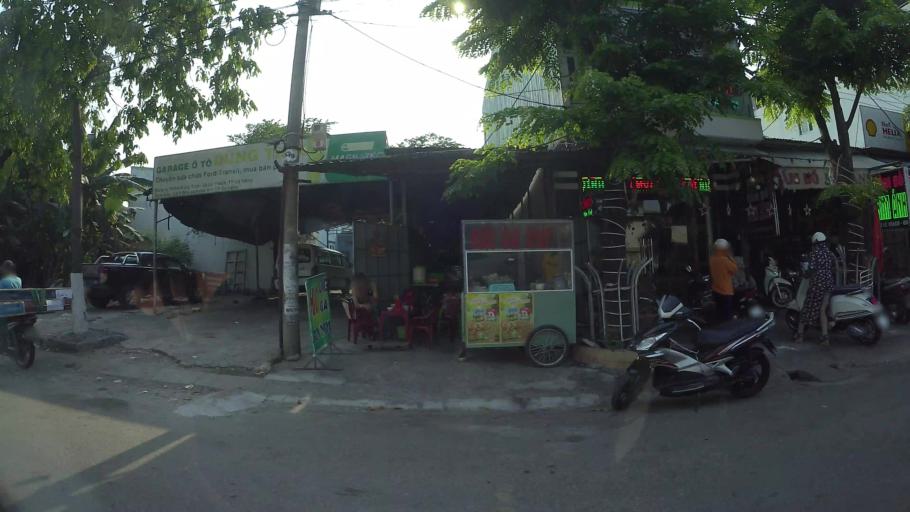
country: VN
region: Da Nang
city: Lien Chieu
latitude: 16.0554
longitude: 108.1723
